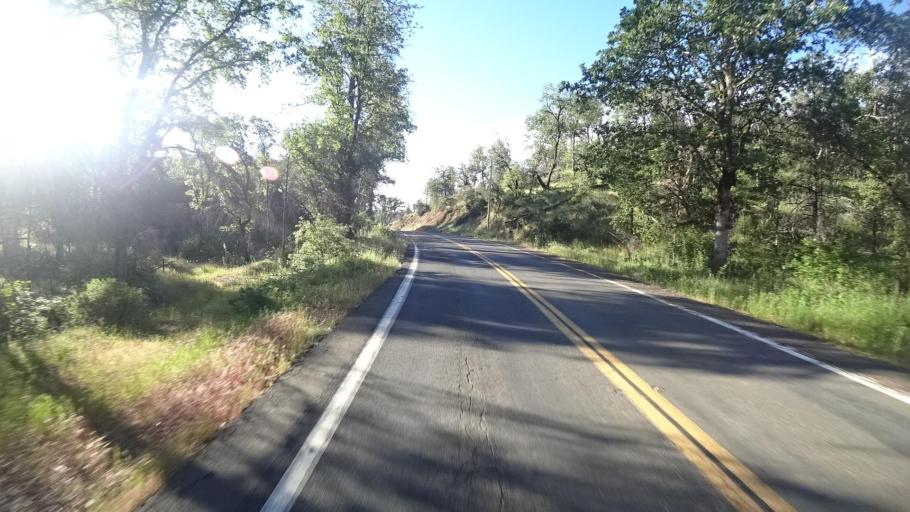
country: US
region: California
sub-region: Lake County
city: Upper Lake
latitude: 39.2091
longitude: -122.9286
